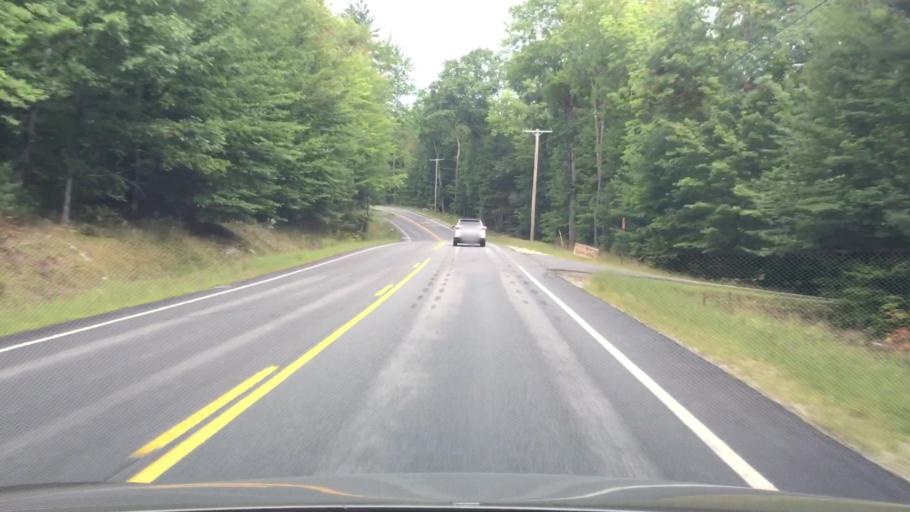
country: US
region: Maine
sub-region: Oxford County
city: Hartford
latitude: 44.3542
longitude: -70.3038
